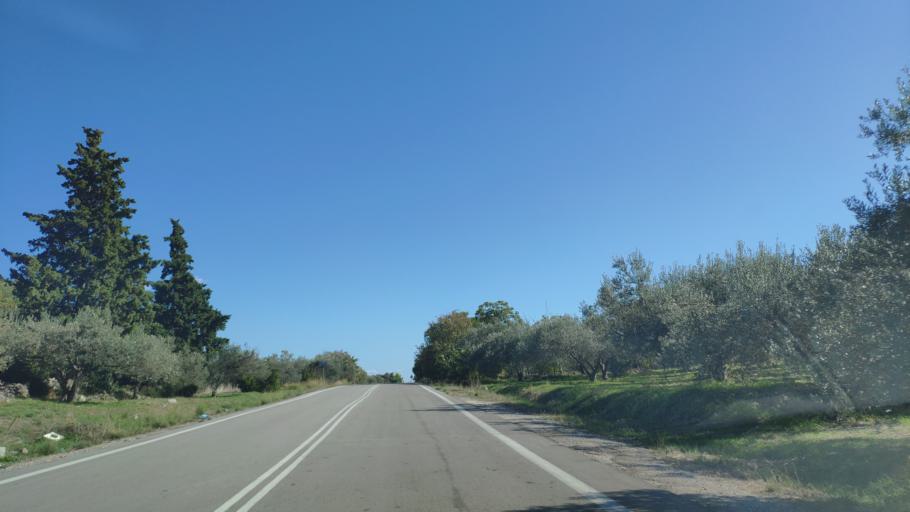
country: GR
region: Peloponnese
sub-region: Nomos Argolidos
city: Palaia Epidavros
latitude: 37.5762
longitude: 23.2447
